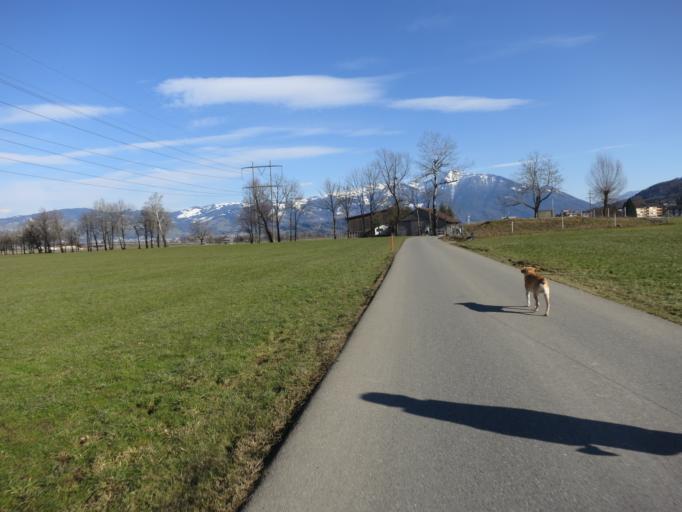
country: CH
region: Schwyz
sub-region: Bezirk March
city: Schubelbach
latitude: 47.1780
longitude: 8.9315
